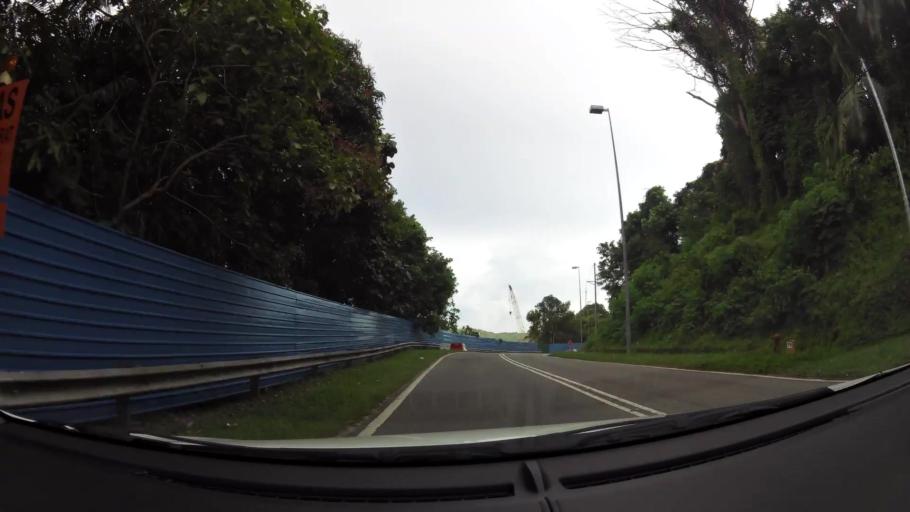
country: BN
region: Brunei and Muara
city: Bandar Seri Begawan
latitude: 4.9303
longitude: 115.0156
